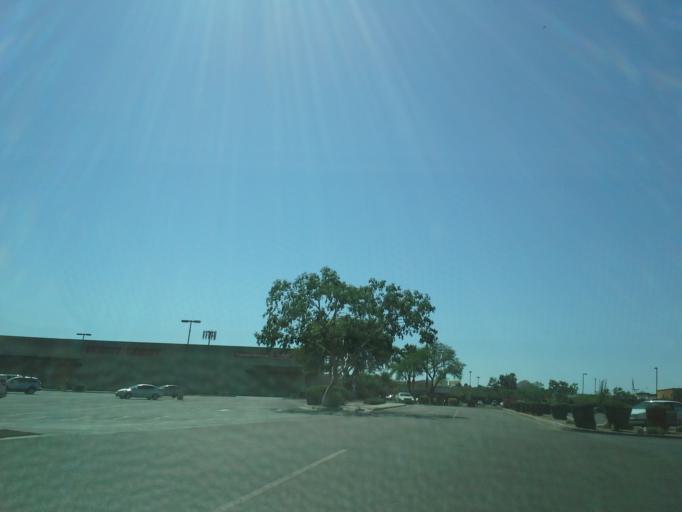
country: US
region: Arizona
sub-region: Maricopa County
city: Paradise Valley
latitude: 33.5979
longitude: -111.9811
